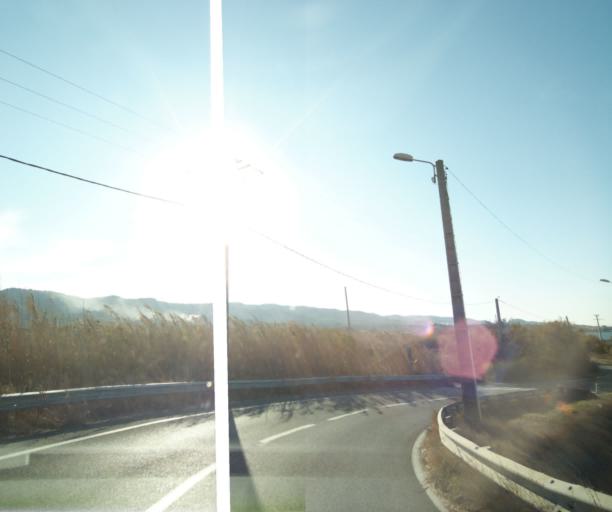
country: FR
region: Provence-Alpes-Cote d'Azur
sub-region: Departement des Bouches-du-Rhone
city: Chateauneuf-les-Martigues
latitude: 43.3992
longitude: 5.1370
